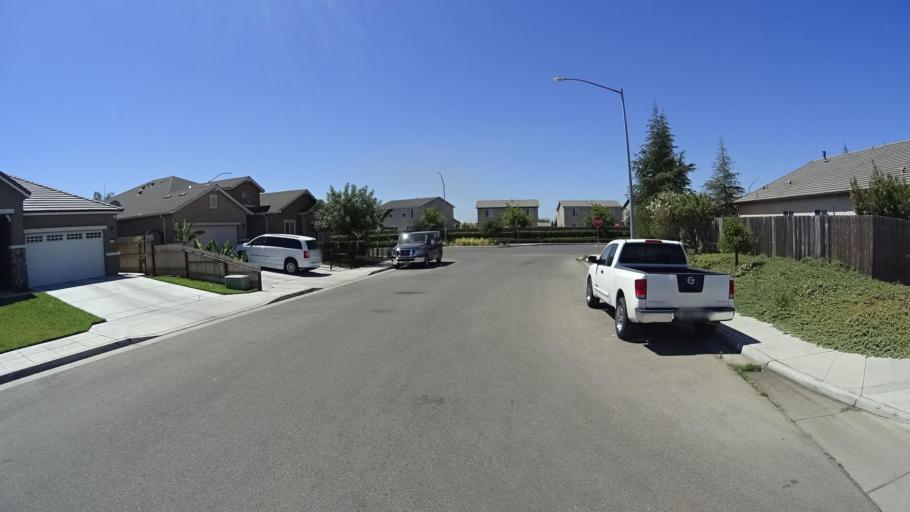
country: US
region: California
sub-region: Fresno County
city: Sunnyside
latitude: 36.7211
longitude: -119.6702
